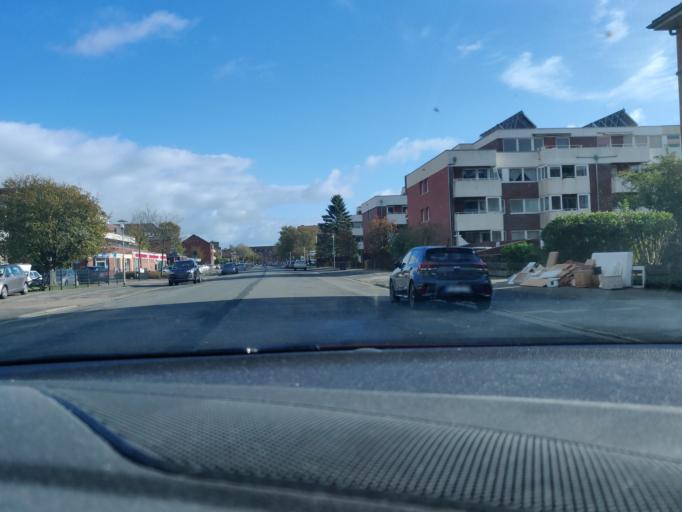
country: DE
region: Lower Saxony
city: Cuxhaven
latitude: 53.8675
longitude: 8.6832
